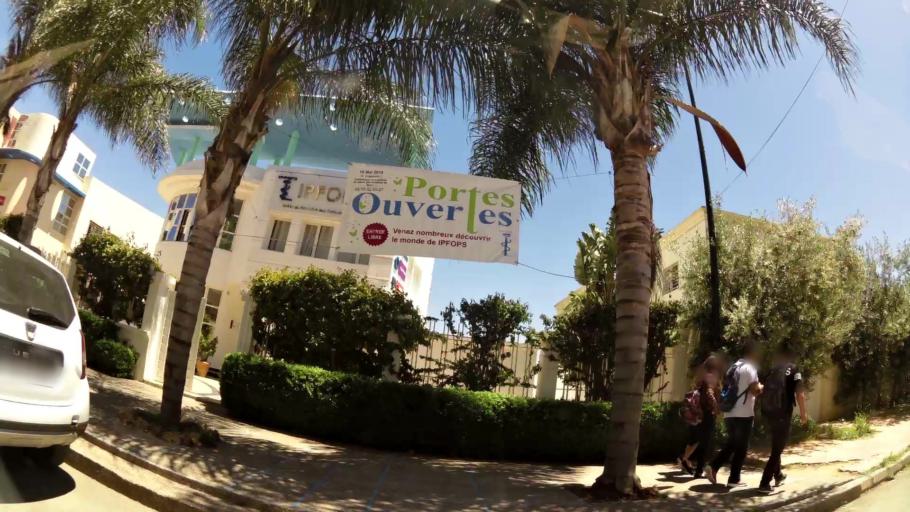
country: MA
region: Meknes-Tafilalet
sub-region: Meknes
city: Meknes
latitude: 33.9044
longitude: -5.5509
